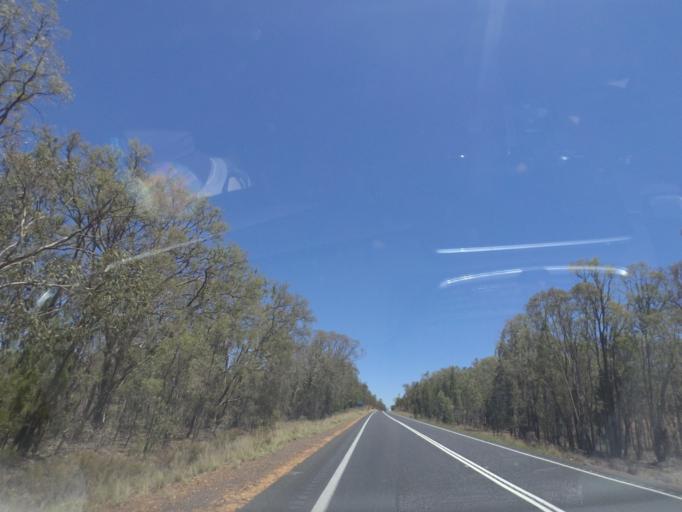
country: AU
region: New South Wales
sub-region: Warrumbungle Shire
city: Coonabarabran
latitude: -31.2274
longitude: 149.3215
